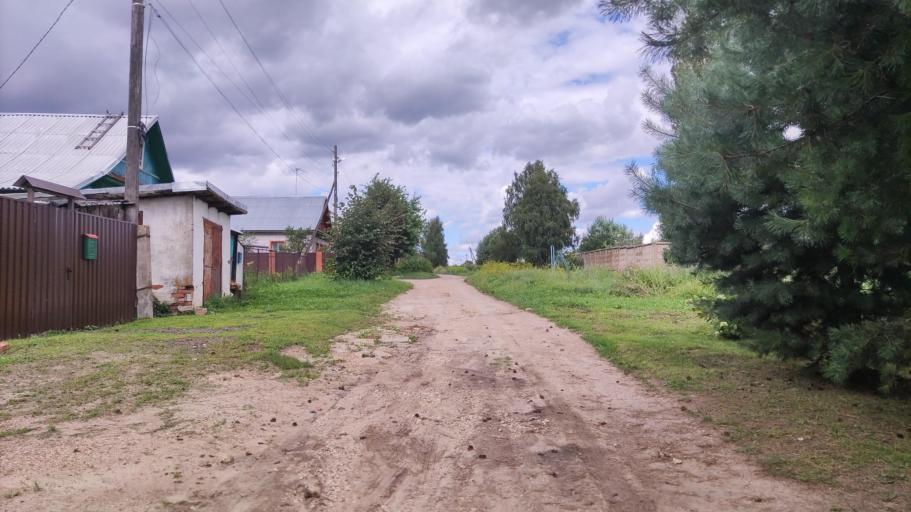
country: RU
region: Tverskaya
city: Rzhev
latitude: 56.2415
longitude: 34.2970
